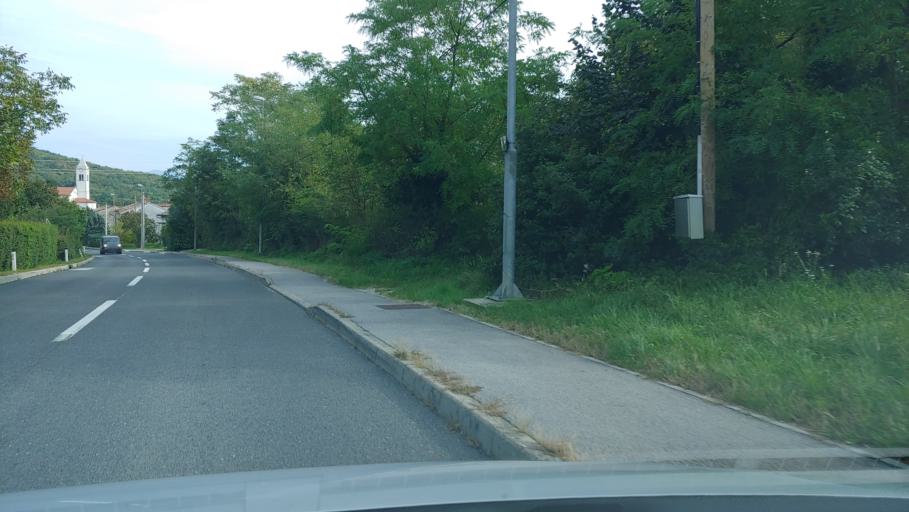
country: SI
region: Nova Gorica
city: Sempas
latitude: 45.9092
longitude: 13.7718
